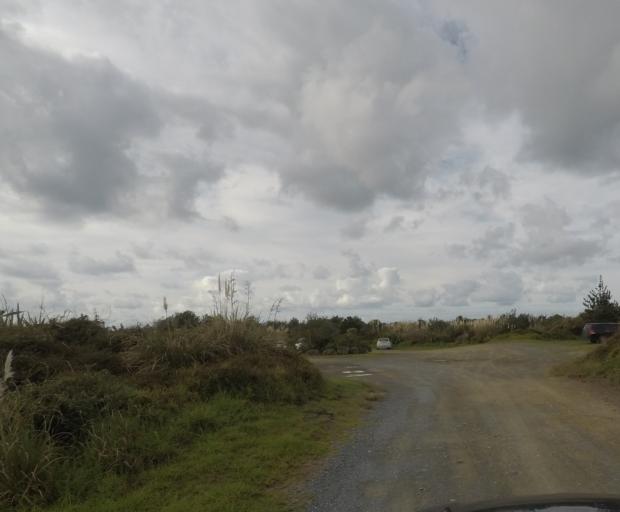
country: NZ
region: Northland
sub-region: Whangarei
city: Ruakaka
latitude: -35.9317
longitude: 174.4597
